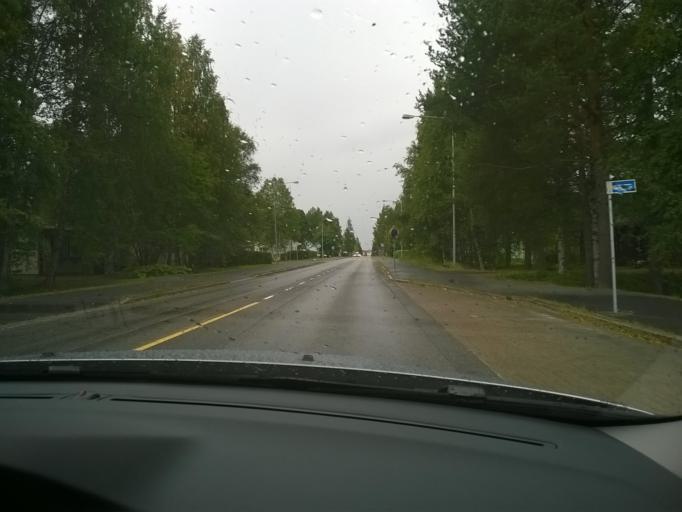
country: FI
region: Kainuu
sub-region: Kehys-Kainuu
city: Kuhmo
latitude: 64.1233
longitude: 29.5348
